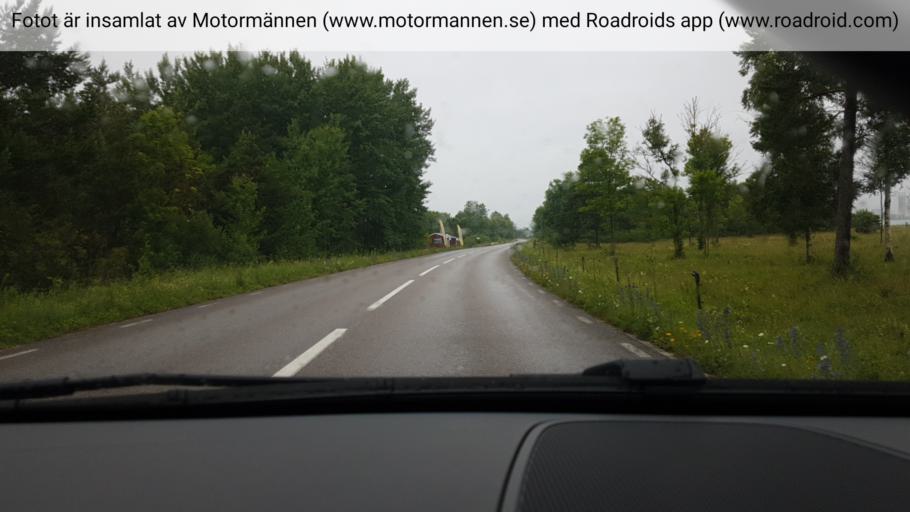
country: SE
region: Gotland
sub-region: Gotland
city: Slite
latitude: 57.8292
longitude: 18.7878
